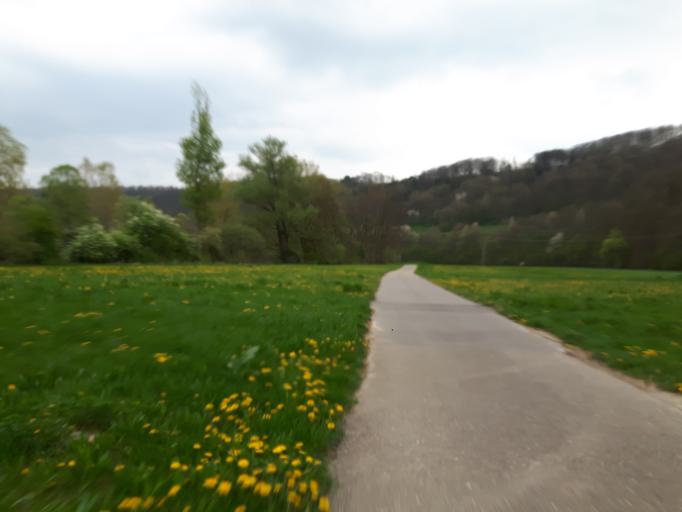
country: DE
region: Baden-Wuerttemberg
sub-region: Regierungsbezirk Stuttgart
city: Weissbach
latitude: 49.2913
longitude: 9.5984
